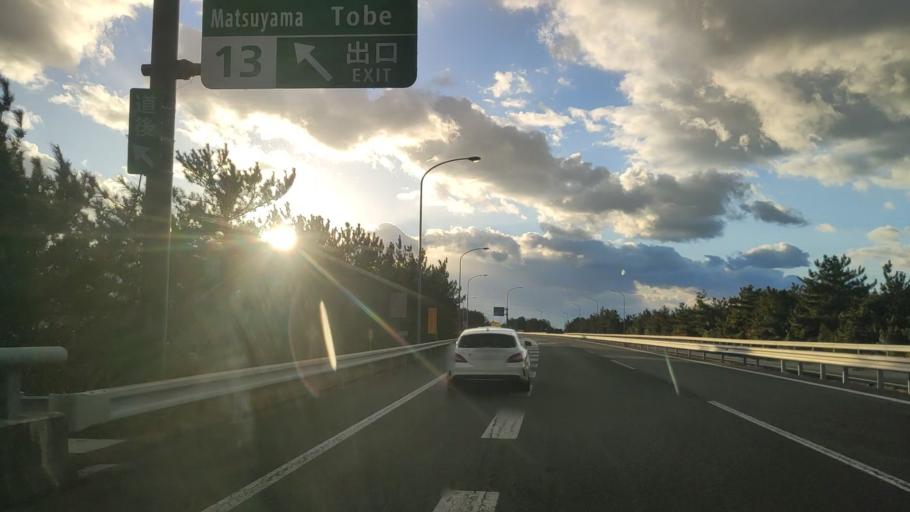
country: JP
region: Ehime
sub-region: Shikoku-chuo Shi
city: Matsuyama
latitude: 33.7960
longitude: 132.7847
